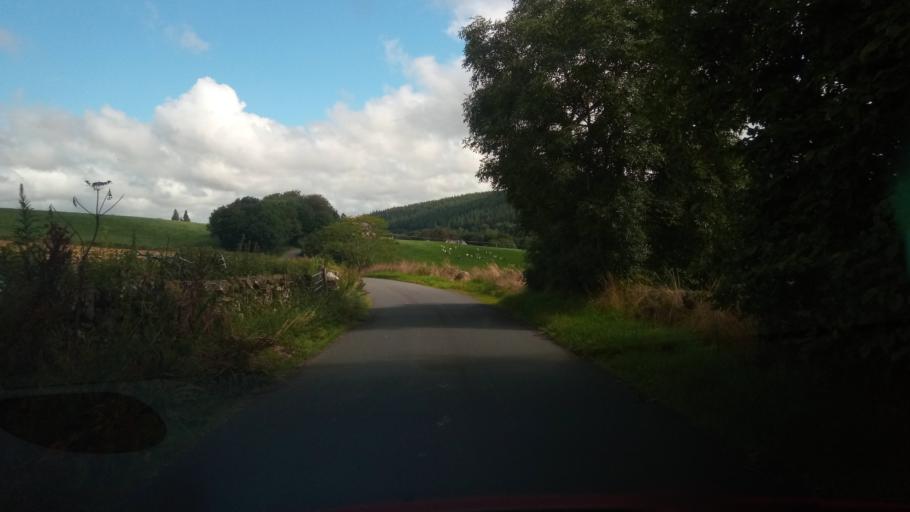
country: GB
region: Scotland
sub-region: The Scottish Borders
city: Earlston
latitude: 55.6419
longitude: -2.7012
